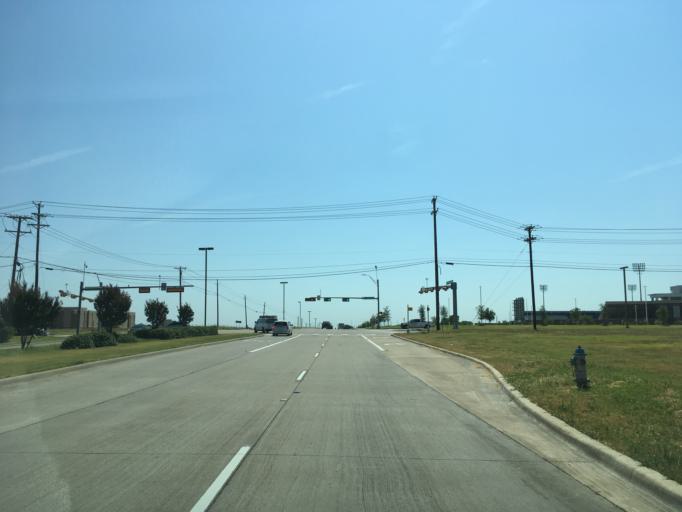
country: US
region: Texas
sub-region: Collin County
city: Fairview
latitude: 33.1589
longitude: -96.6643
